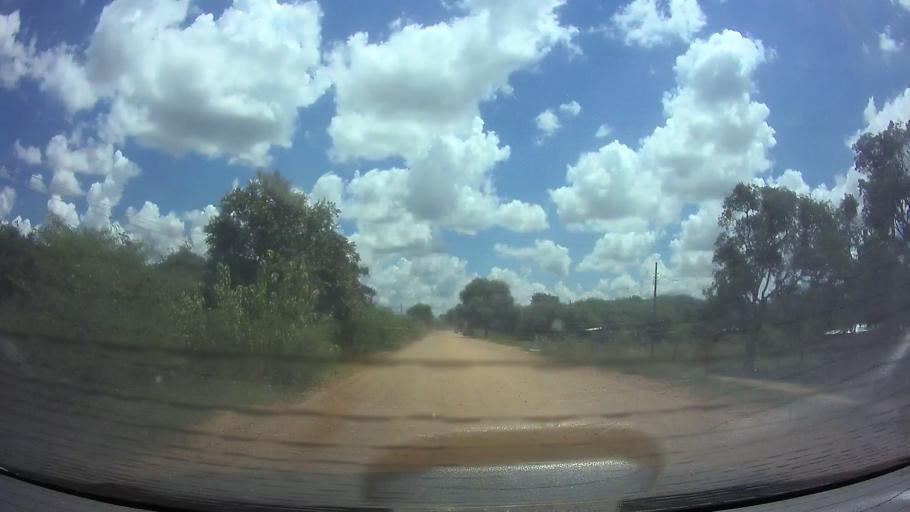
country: PY
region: Presidente Hayes
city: Nanawa
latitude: -25.2487
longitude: -57.6510
